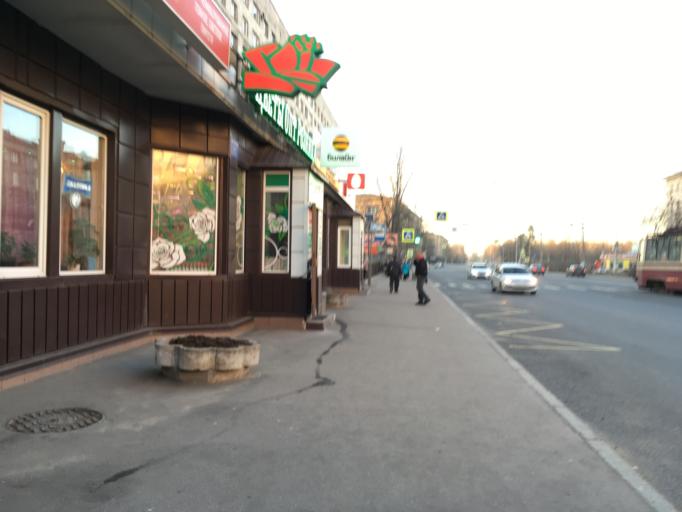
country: RU
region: St.-Petersburg
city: Kushelevka
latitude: 60.0002
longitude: 30.3652
